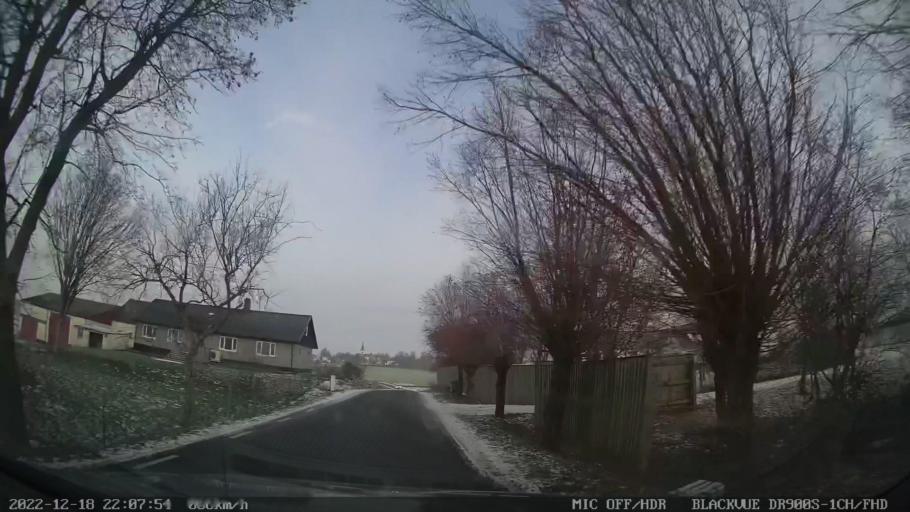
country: SE
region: Skane
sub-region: Tomelilla Kommun
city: Tomelilla
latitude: 55.5213
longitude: 14.0433
